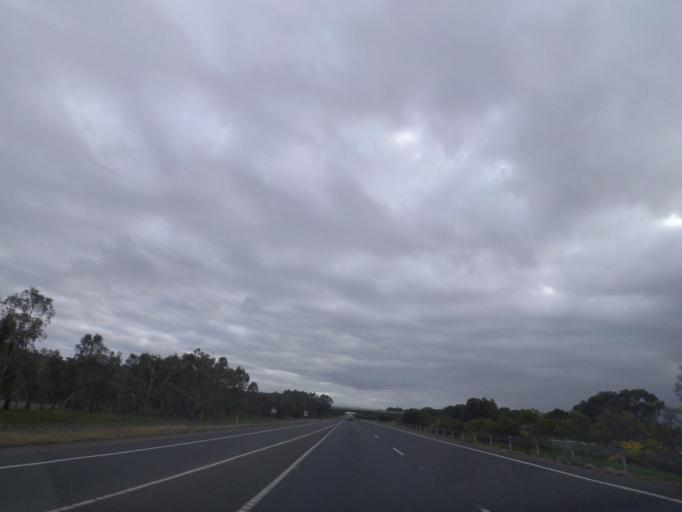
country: AU
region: New South Wales
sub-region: Corowa Shire
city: Howlong
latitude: -36.0820
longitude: 146.7316
